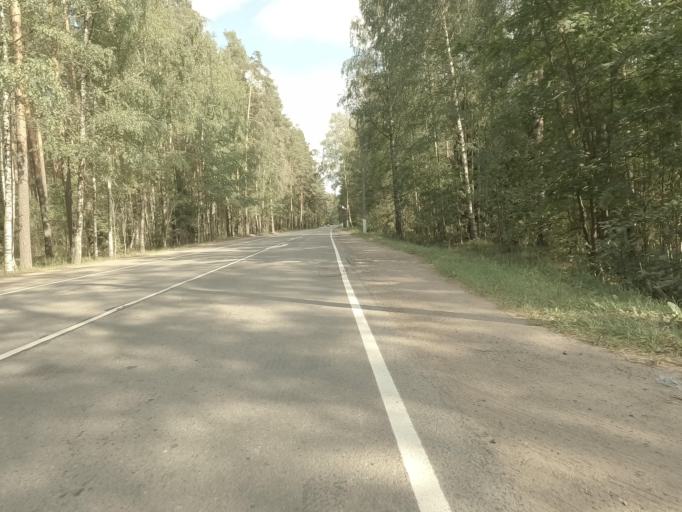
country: RU
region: Leningrad
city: Kamennogorsk
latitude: 60.9450
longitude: 29.1442
